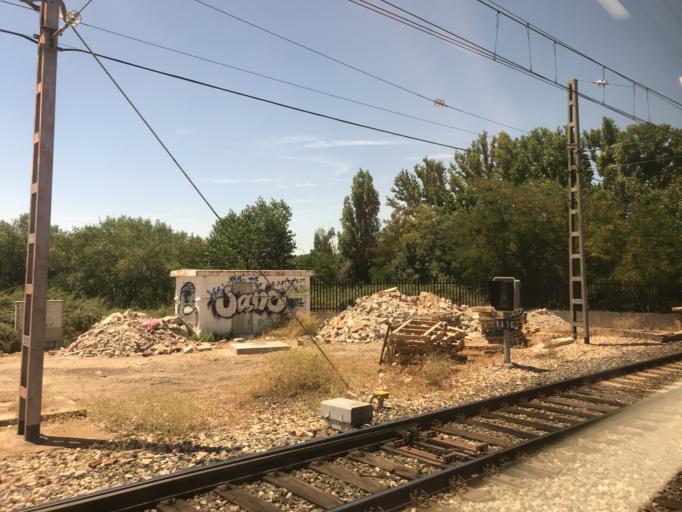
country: ES
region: Madrid
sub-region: Provincia de Madrid
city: Aranjuez
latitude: 40.0376
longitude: -3.6191
